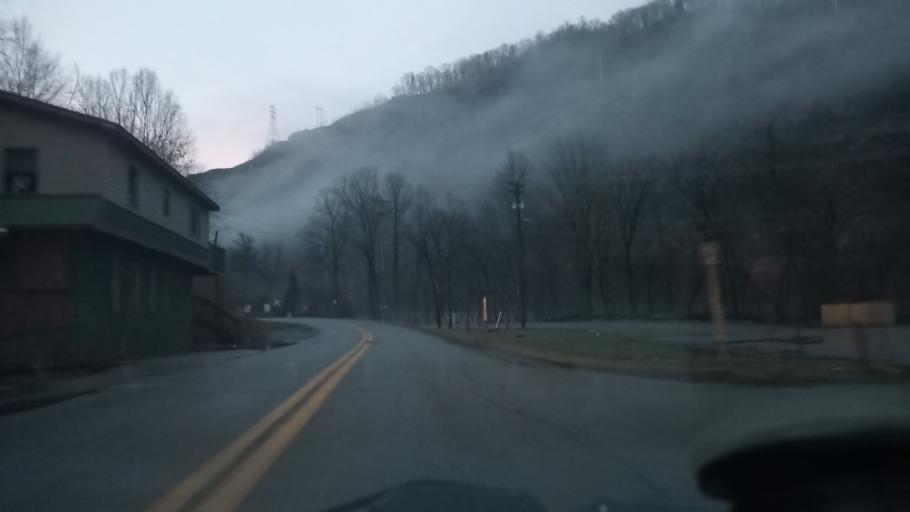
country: US
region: West Virginia
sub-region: Logan County
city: Mallory
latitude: 37.7338
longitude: -81.8752
